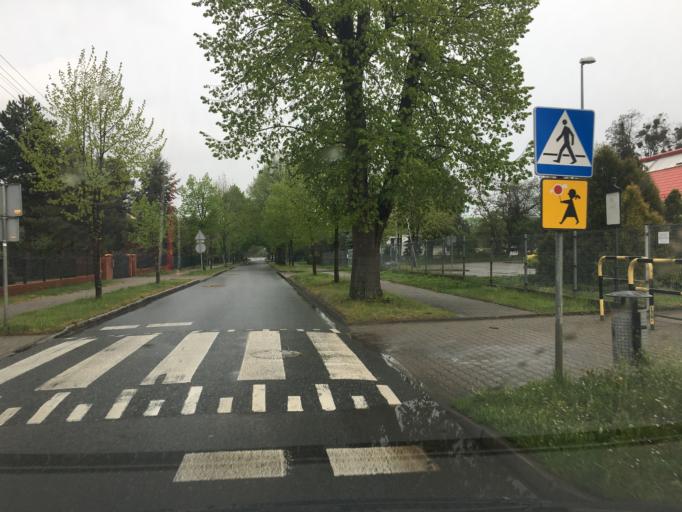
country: PL
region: Lower Silesian Voivodeship
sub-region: Powiat wroclawski
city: Zerniki Wroclawskie
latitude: 51.0311
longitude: 17.0611
